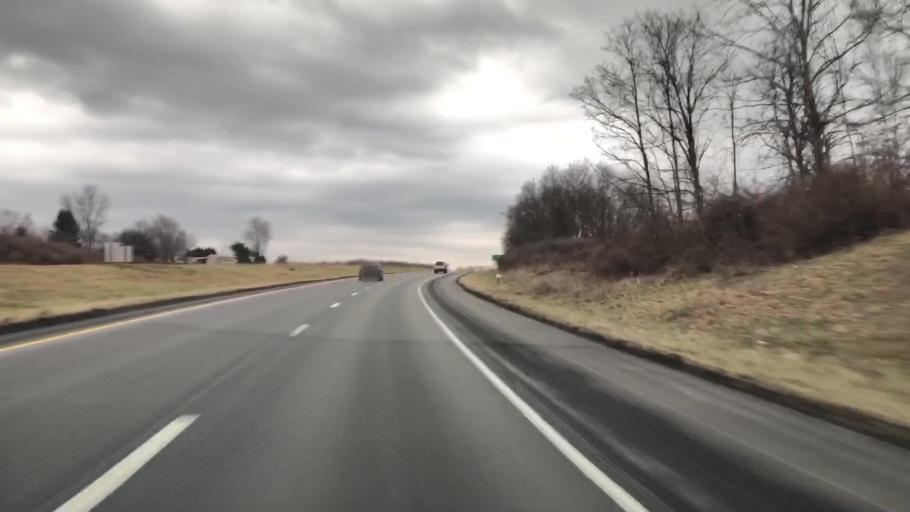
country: US
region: Pennsylvania
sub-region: Butler County
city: Slippery Rock
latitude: 41.0331
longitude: -80.1208
